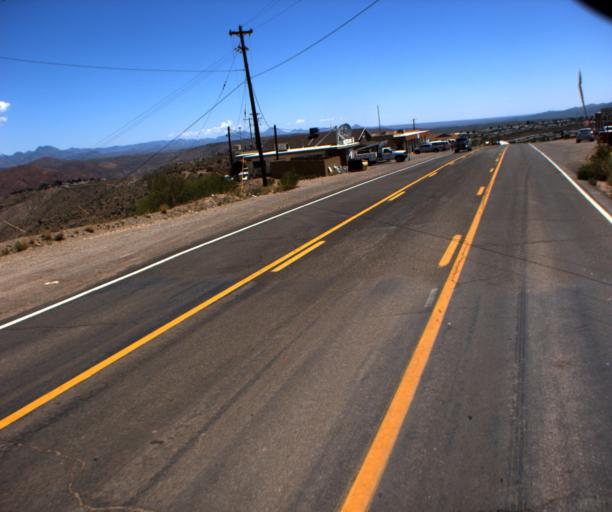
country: US
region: Arizona
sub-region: Greenlee County
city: Clifton
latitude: 33.0568
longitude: -109.3286
